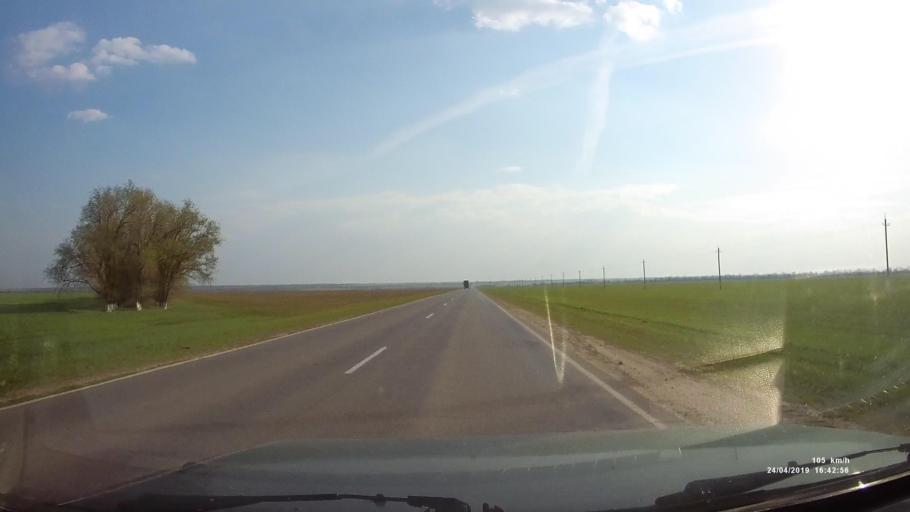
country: RU
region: Rostov
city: Gundorovskiy
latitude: 46.8009
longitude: 41.8472
